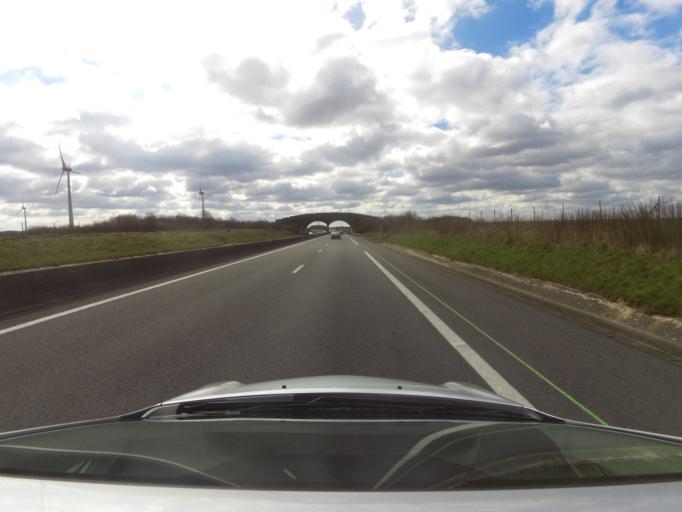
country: FR
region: Picardie
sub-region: Departement de la Somme
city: Rue
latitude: 50.3045
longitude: 1.7250
